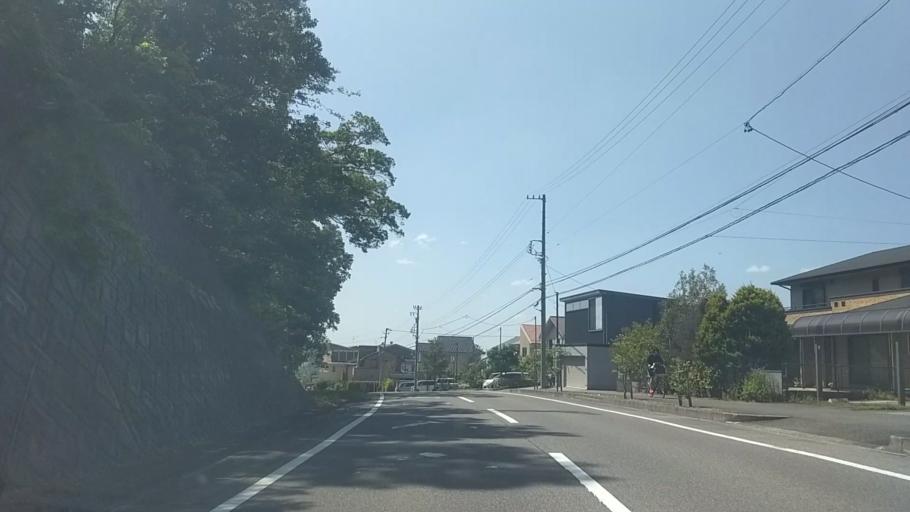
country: JP
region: Aichi
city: Okazaki
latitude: 34.9728
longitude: 137.1899
